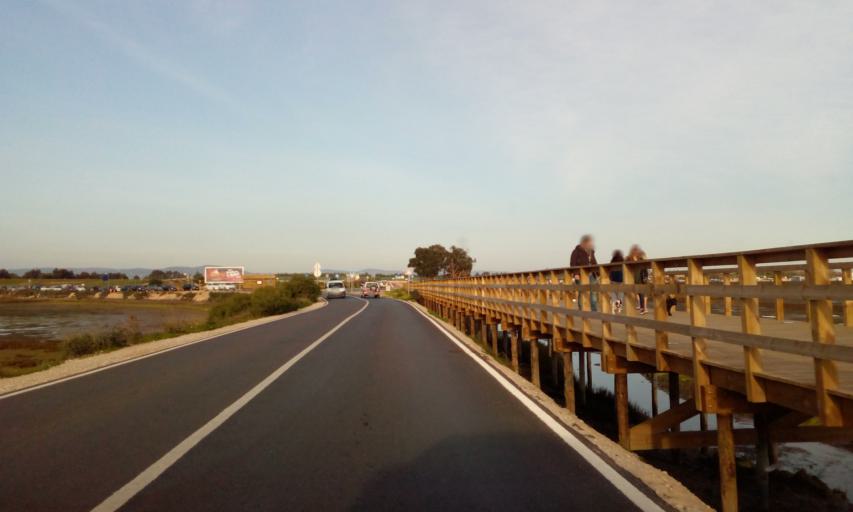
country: PT
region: Faro
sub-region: Faro
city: Faro
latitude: 37.0136
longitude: -7.9888
